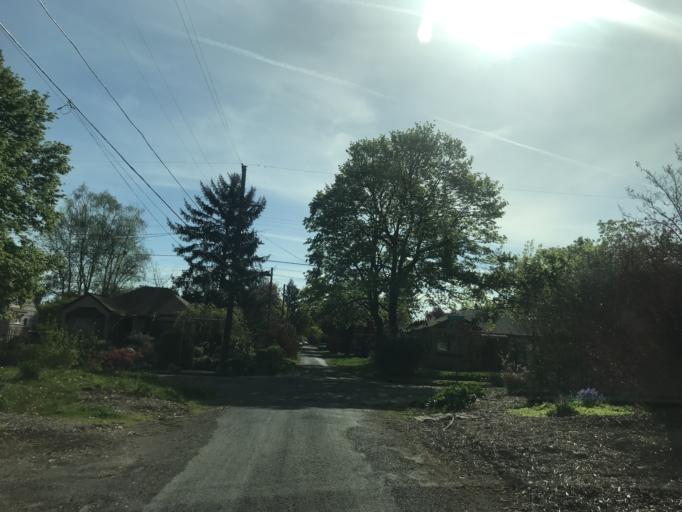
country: US
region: Oregon
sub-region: Multnomah County
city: Lents
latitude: 45.4987
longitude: -122.5854
